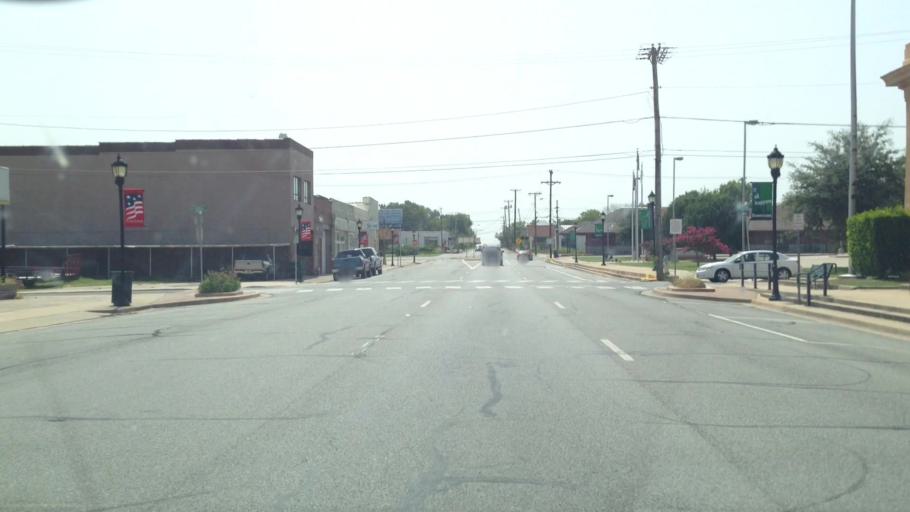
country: US
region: Texas
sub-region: Hunt County
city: Greenville
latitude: 33.1399
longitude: -96.1106
